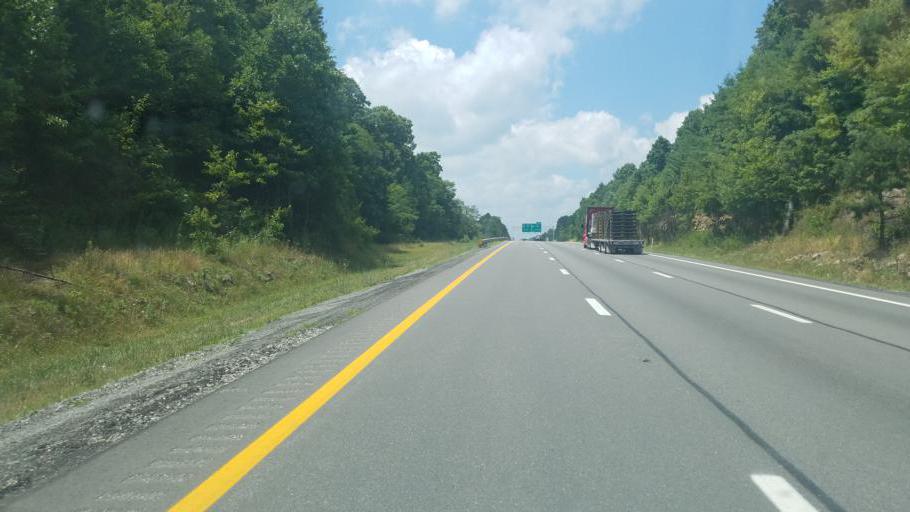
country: US
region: West Virginia
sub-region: Raleigh County
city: MacArthur
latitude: 37.7244
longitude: -81.1836
